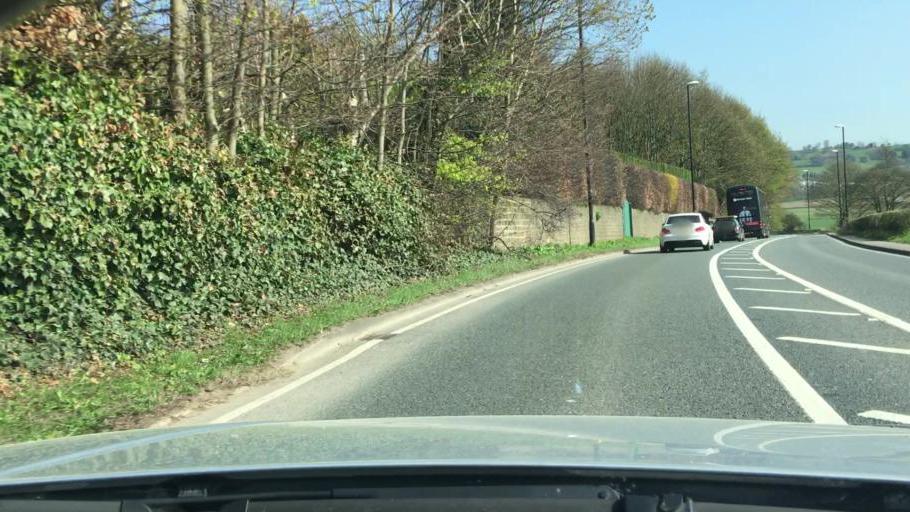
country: GB
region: England
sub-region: City and Borough of Leeds
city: East Keswick
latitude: 53.9041
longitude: -1.5117
